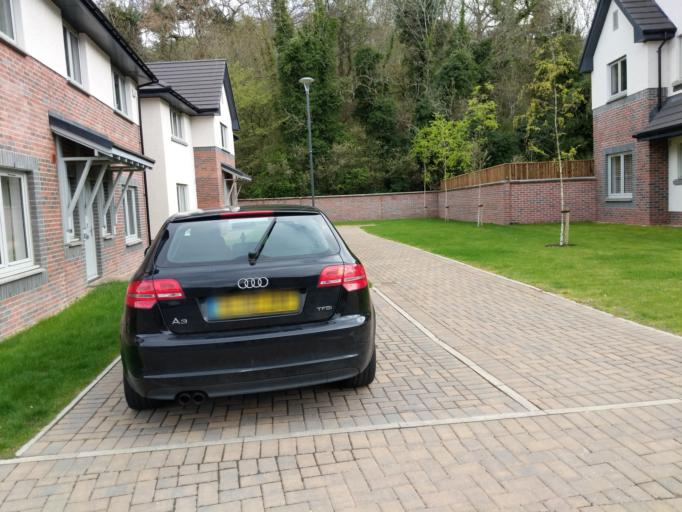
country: GB
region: Scotland
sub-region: Edinburgh
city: Currie
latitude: 55.8982
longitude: -3.2972
